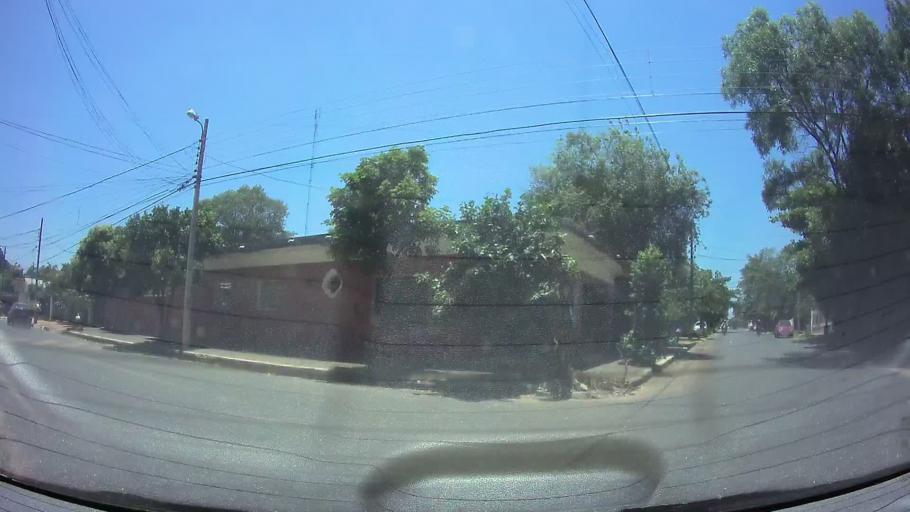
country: PY
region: Central
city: San Lorenzo
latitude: -25.2738
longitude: -57.5085
